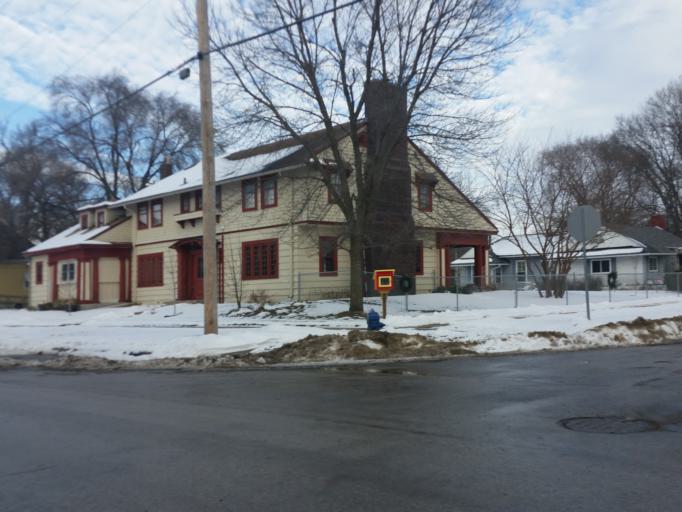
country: US
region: Iowa
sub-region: Black Hawk County
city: Waterloo
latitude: 42.5036
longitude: -92.3344
